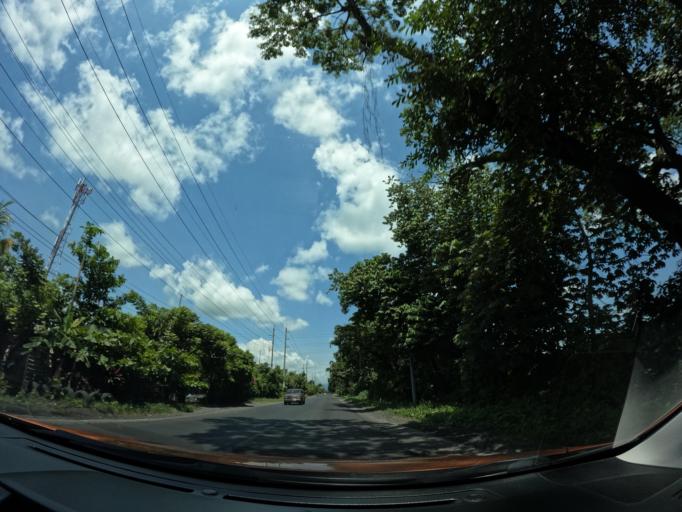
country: GT
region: Escuintla
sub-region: Municipio de Masagua
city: Masagua
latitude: 14.2254
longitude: -90.8280
